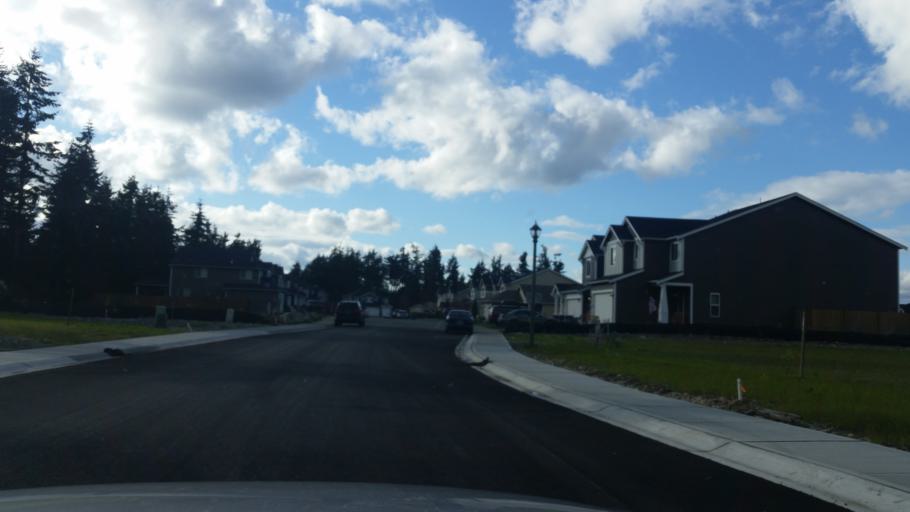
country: US
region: Washington
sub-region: Pierce County
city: Graham
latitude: 47.0843
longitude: -122.2763
